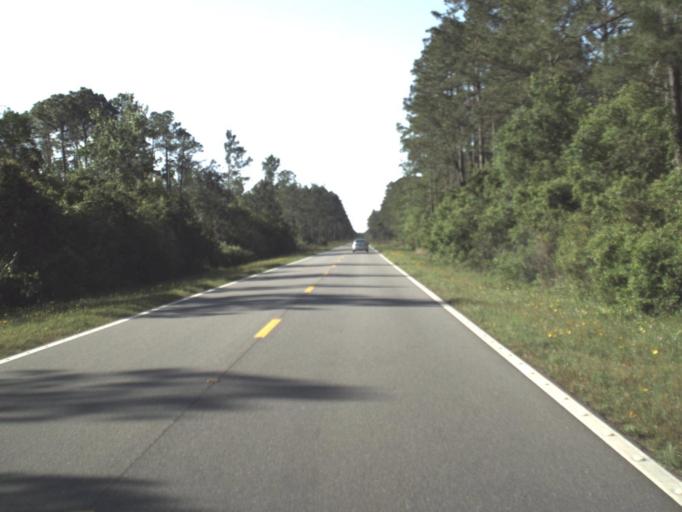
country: US
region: Florida
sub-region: Gulf County
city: Wewahitchka
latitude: 30.1077
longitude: -84.9866
